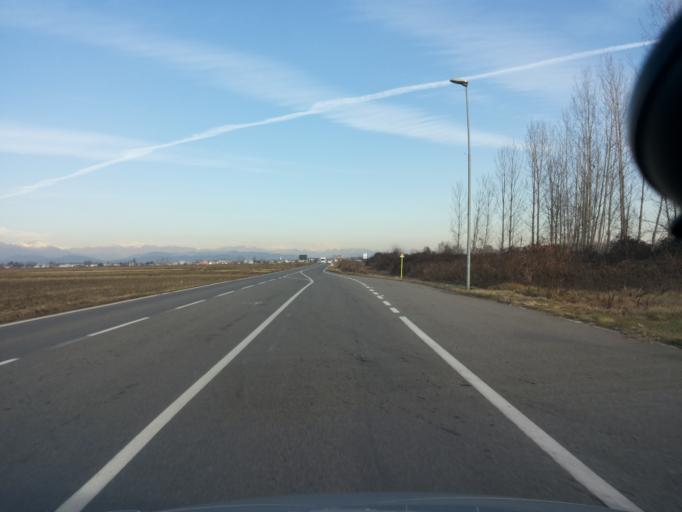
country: IT
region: Piedmont
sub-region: Provincia di Vercelli
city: Arborio
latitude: 45.4761
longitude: 8.3876
